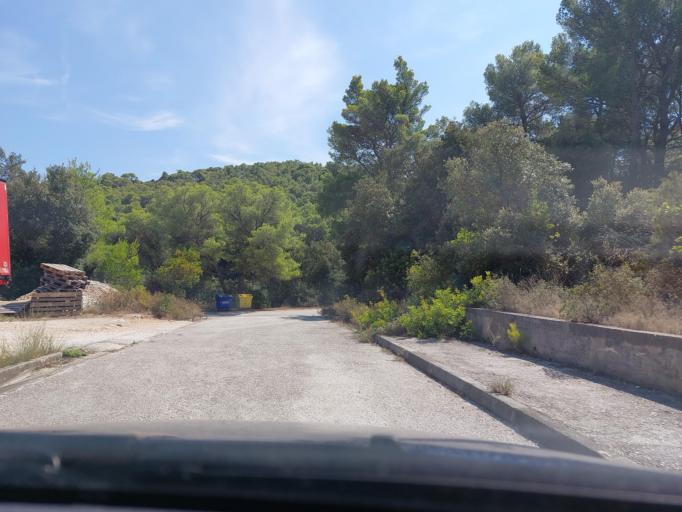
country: HR
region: Dubrovacko-Neretvanska
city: Smokvica
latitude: 42.7426
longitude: 16.8256
